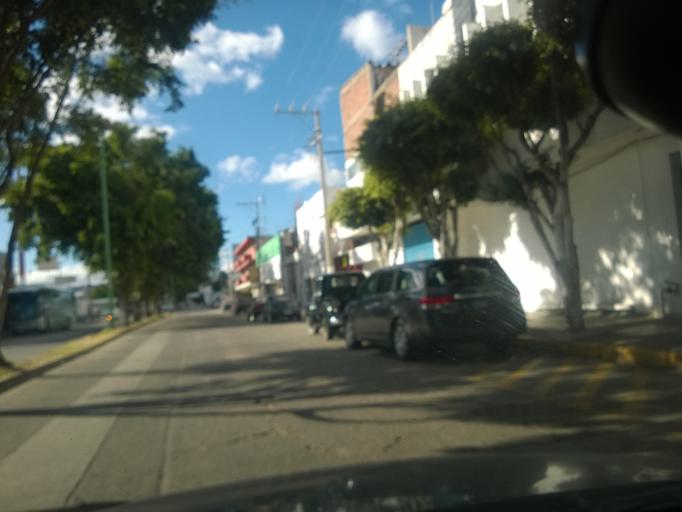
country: MX
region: Guanajuato
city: Leon
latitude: 21.1393
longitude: -101.6843
